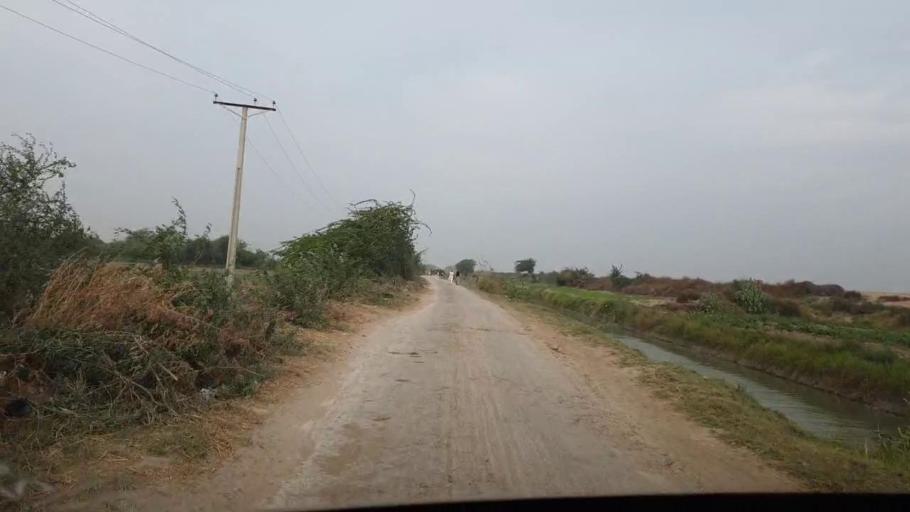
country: PK
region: Sindh
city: Chuhar Jamali
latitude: 24.4017
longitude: 67.9636
